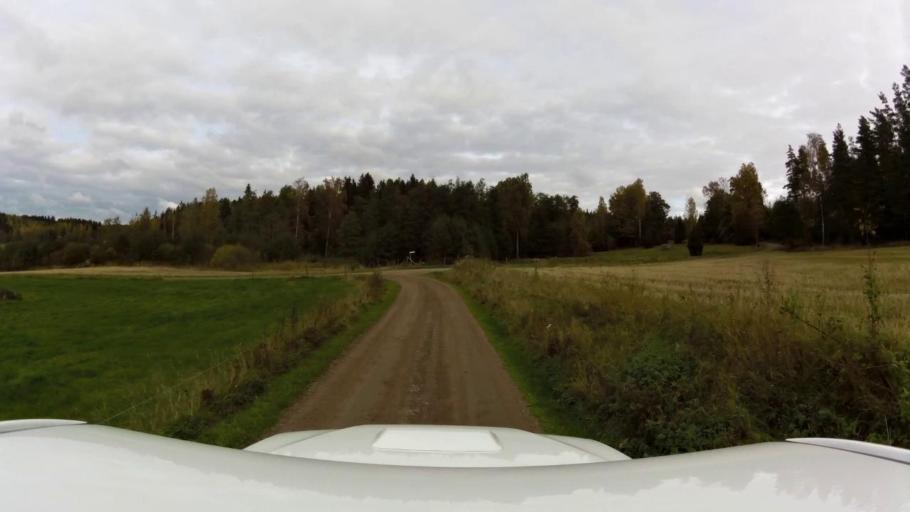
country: SE
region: OEstergoetland
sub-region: Linkopings Kommun
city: Ekangen
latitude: 58.5625
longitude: 15.6672
